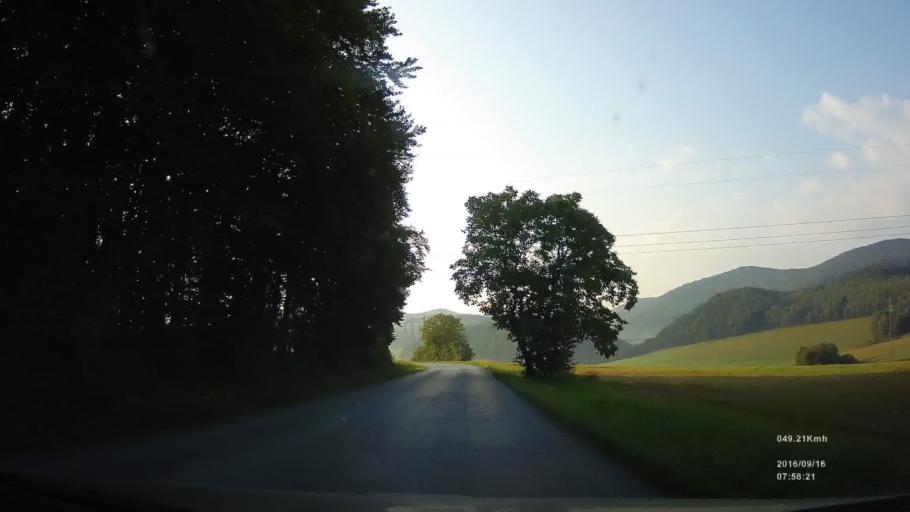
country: SK
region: Presovsky
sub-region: Okres Presov
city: Presov
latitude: 48.9099
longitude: 21.1524
